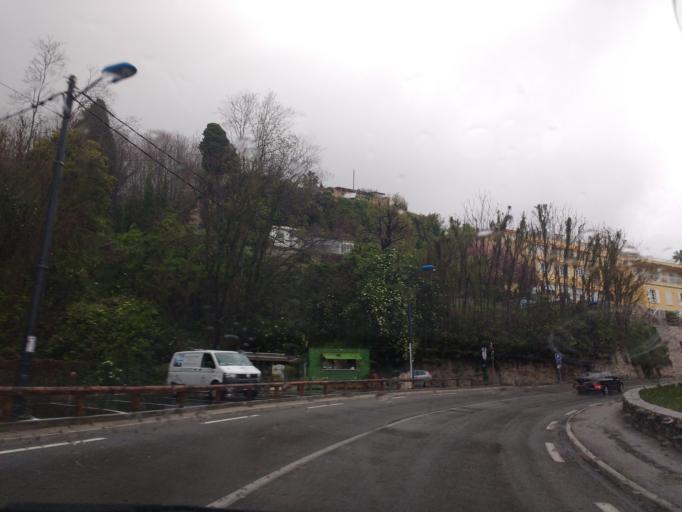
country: FR
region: Provence-Alpes-Cote d'Azur
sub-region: Departement des Alpes-Maritimes
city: Eze
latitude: 43.7247
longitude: 7.3798
